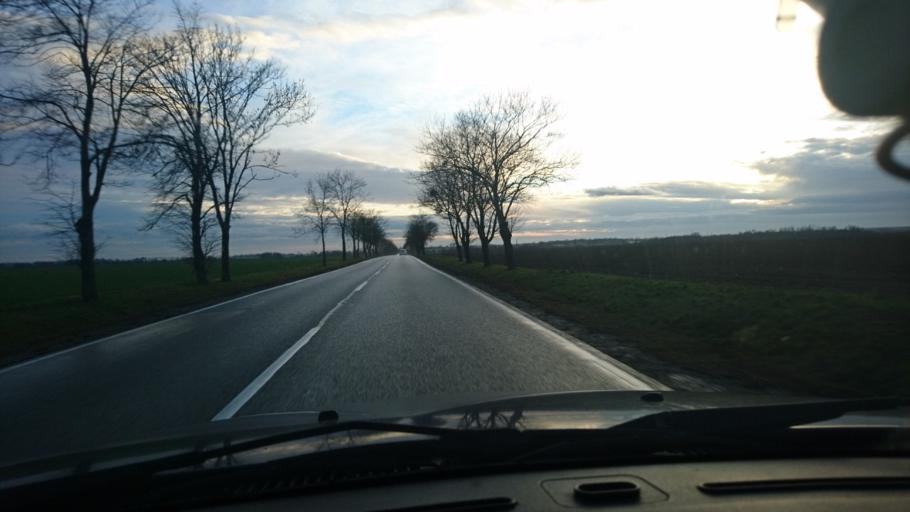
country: PL
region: Opole Voivodeship
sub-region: Powiat kluczborski
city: Byczyna
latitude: 51.0958
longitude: 18.2031
